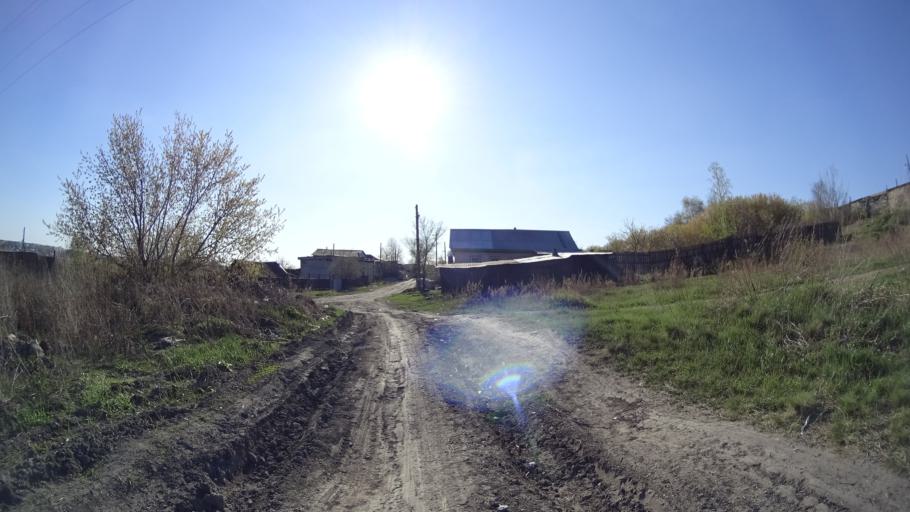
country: RU
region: Chelyabinsk
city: Troitsk
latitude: 54.0992
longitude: 61.5504
